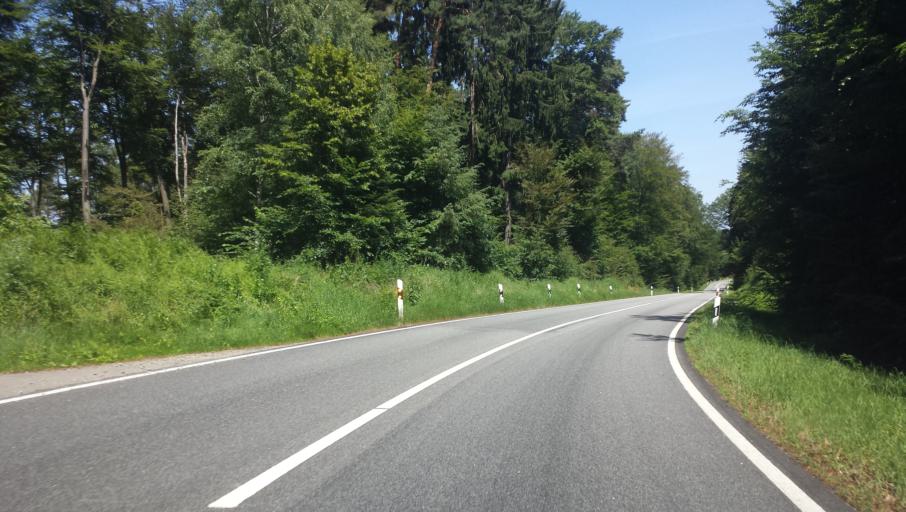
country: DE
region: Rheinland-Pfalz
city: Waldleiningen
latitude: 49.4073
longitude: 7.8648
